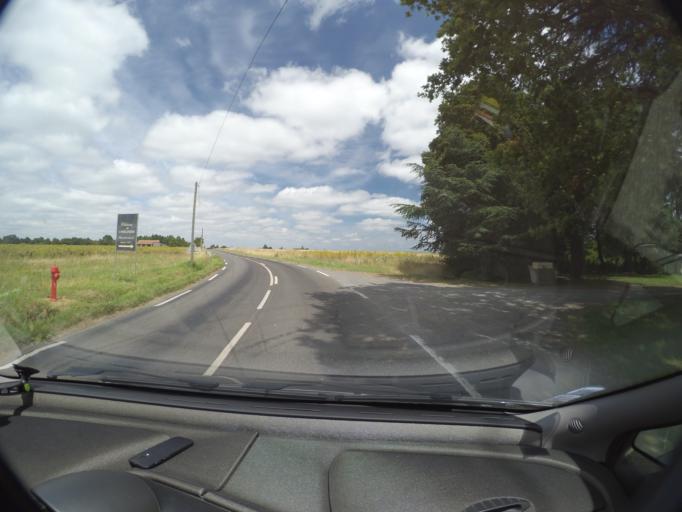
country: FR
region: Pays de la Loire
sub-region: Departement de la Loire-Atlantique
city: Gorges
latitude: 47.1094
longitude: -1.2962
